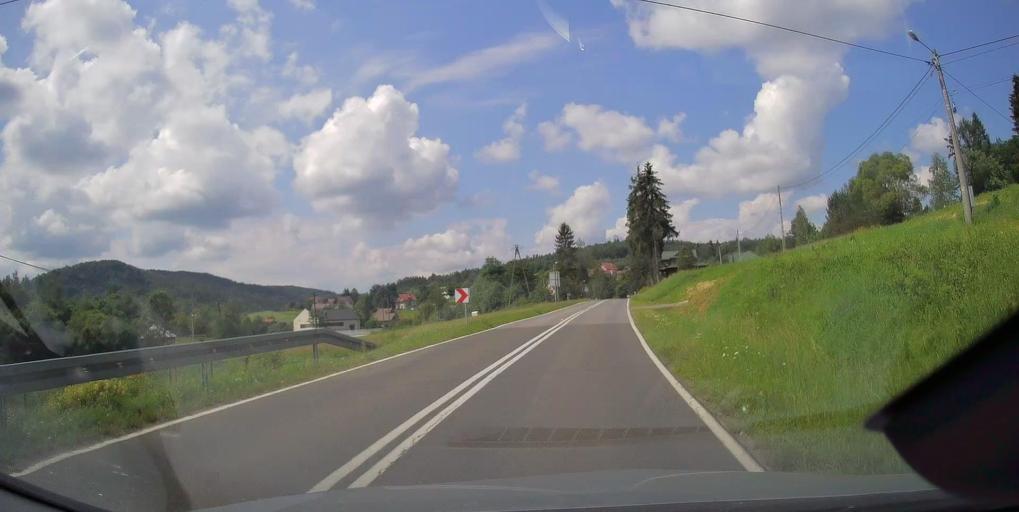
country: PL
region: Lesser Poland Voivodeship
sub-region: Powiat tarnowski
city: Zakliczyn
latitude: 49.7920
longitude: 20.7993
